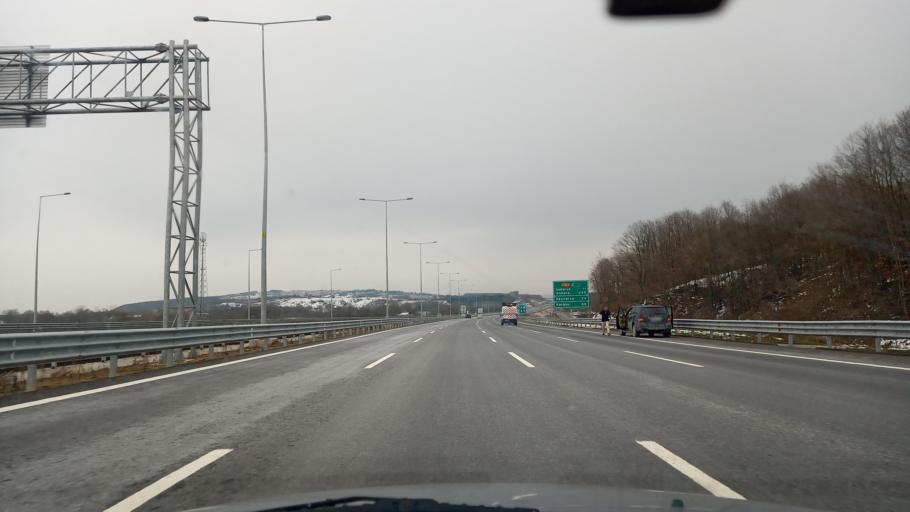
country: TR
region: Kocaeli
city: Akmese
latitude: 40.8472
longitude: 30.2305
